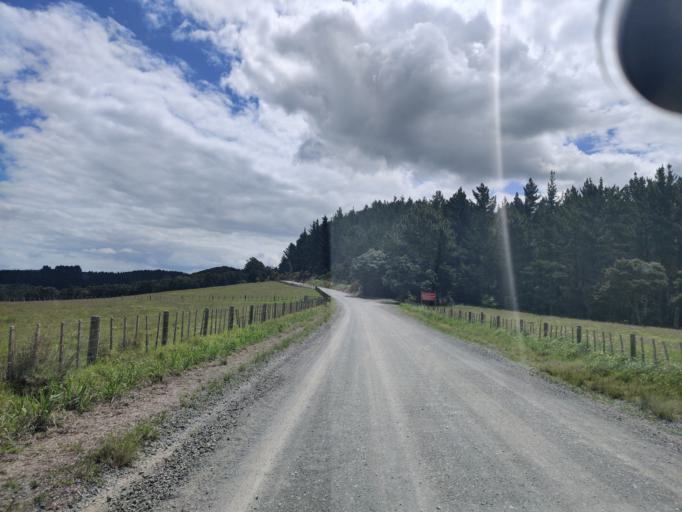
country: NZ
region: Northland
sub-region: Far North District
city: Paihia
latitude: -35.2594
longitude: 174.0663
